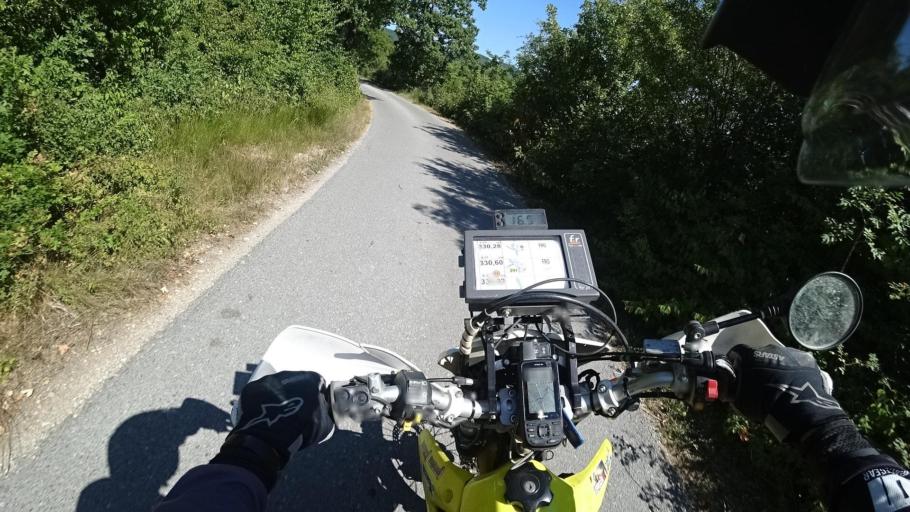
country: HR
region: Licko-Senjska
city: Otocac
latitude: 44.7449
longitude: 15.3887
